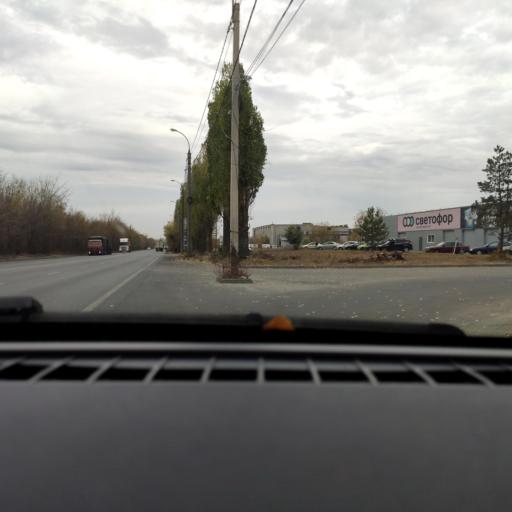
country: RU
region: Voronezj
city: Maslovka
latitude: 51.6050
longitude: 39.2548
